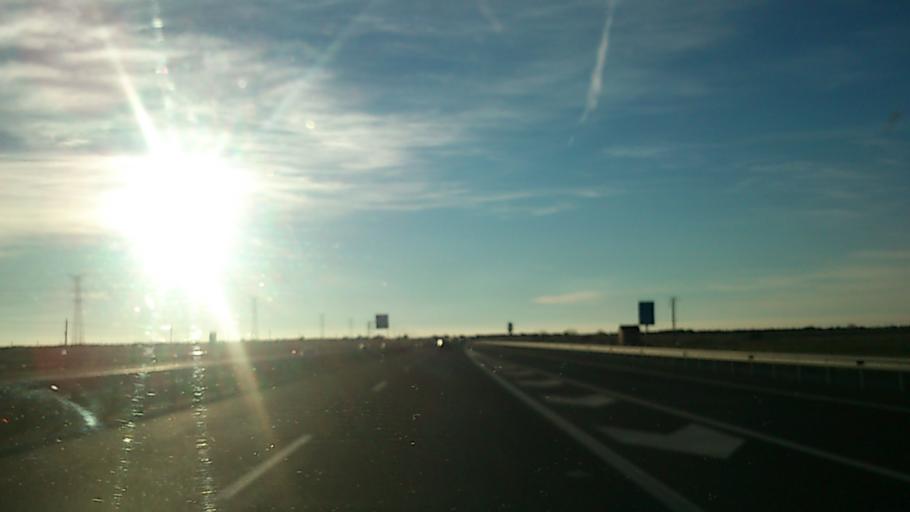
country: ES
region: Castille-La Mancha
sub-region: Provincia de Guadalajara
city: Ledanca
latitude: 40.8557
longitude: -2.8443
